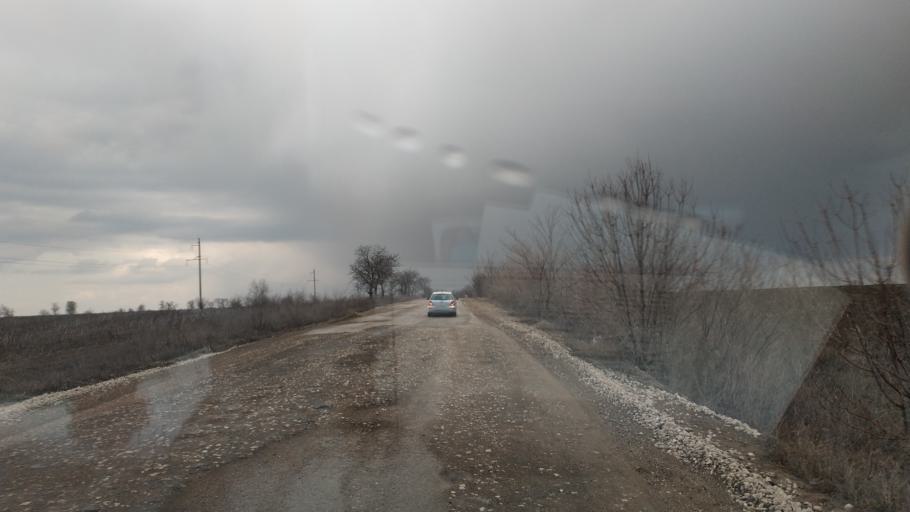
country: MD
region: Telenesti
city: Grigoriopol
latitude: 47.0643
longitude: 29.2988
